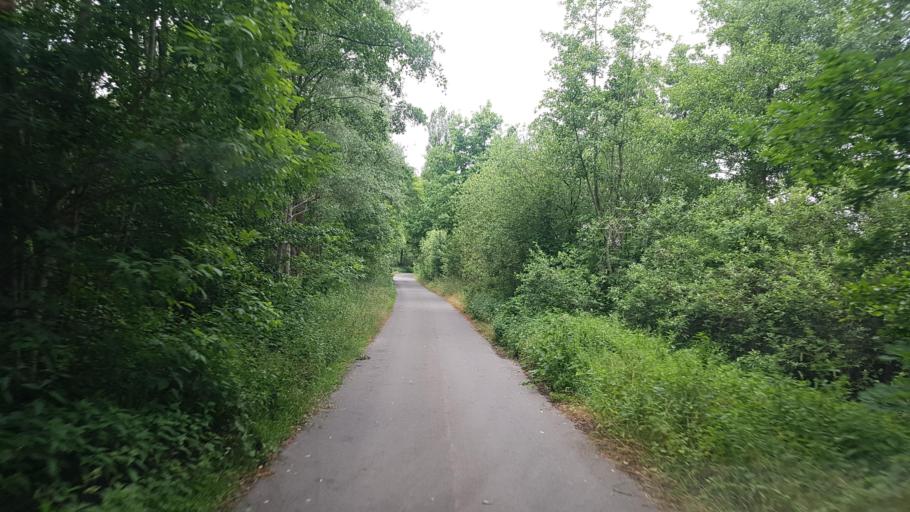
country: DE
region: Brandenburg
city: Grossthiemig
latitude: 51.4003
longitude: 13.6449
